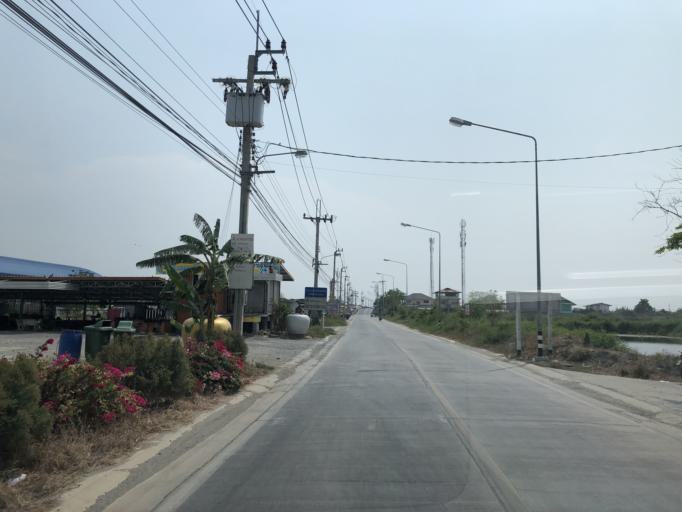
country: TH
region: Samut Prakan
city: Bang Bo
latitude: 13.5323
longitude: 100.8723
